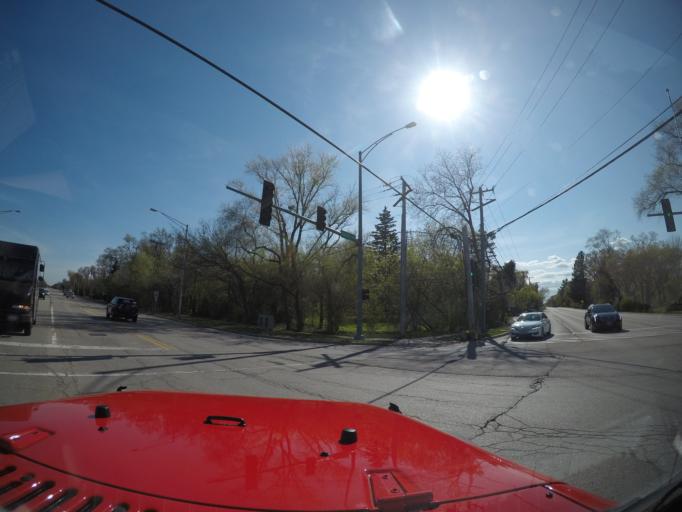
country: US
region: Illinois
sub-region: Cook County
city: Northbrook
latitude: 42.1164
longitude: -87.8294
